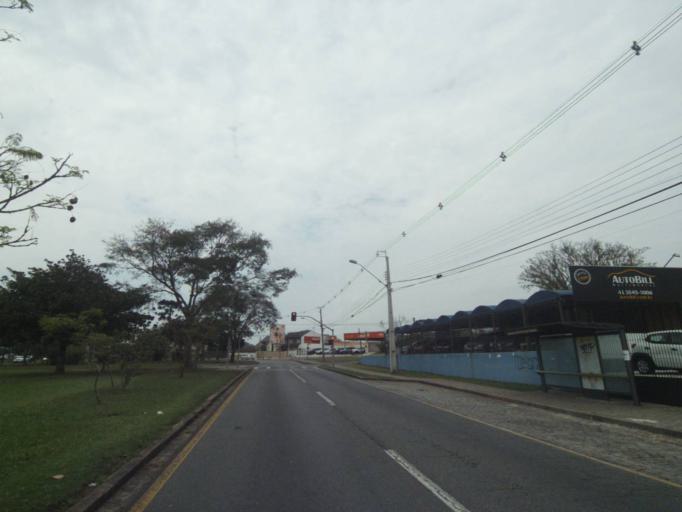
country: BR
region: Parana
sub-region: Curitiba
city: Curitiba
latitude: -25.4658
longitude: -49.3007
